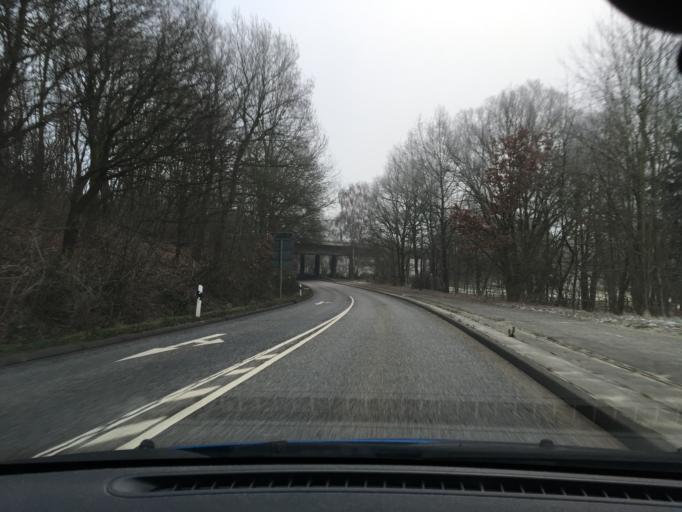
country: DE
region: Lower Saxony
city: Seevetal
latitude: 53.4202
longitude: 9.9700
